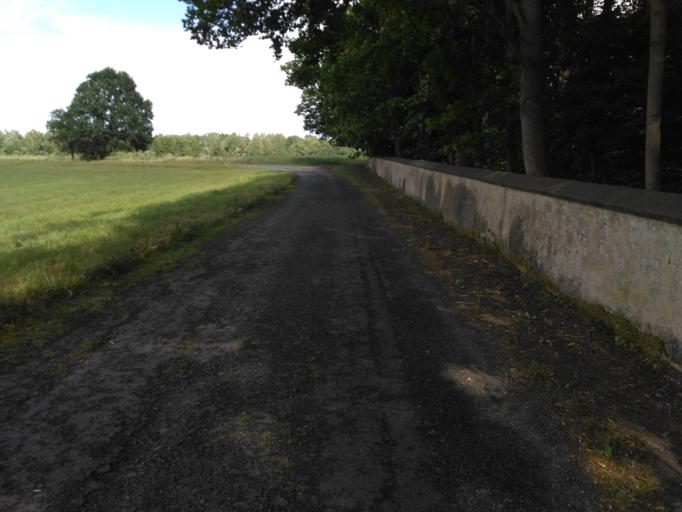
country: DE
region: Saxony
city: Tauscha
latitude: 51.2969
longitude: 13.8314
